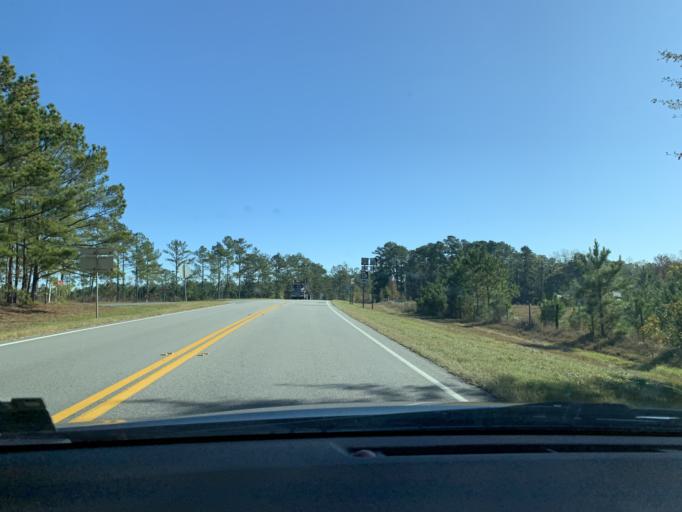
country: US
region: Georgia
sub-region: Ben Hill County
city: Fitzgerald
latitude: 31.7785
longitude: -83.0817
